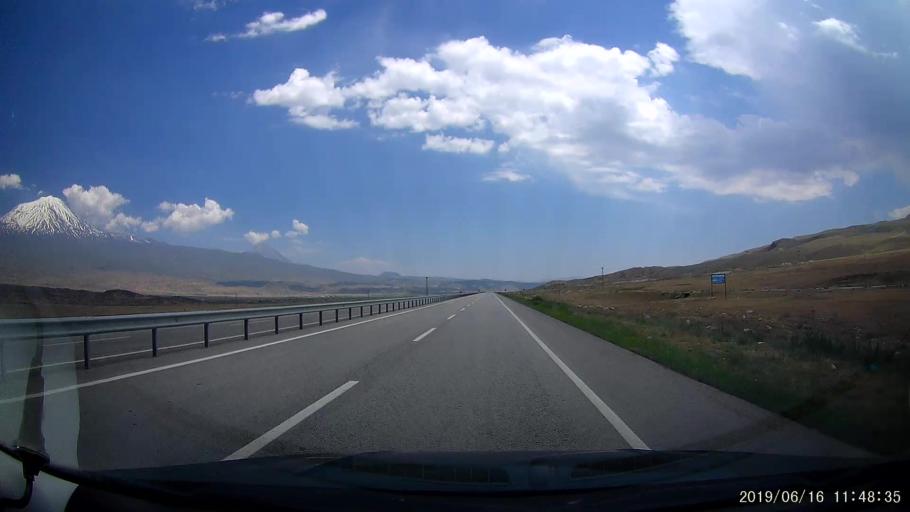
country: TR
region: Agri
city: Dogubayazit
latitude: 39.5579
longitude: 44.1466
